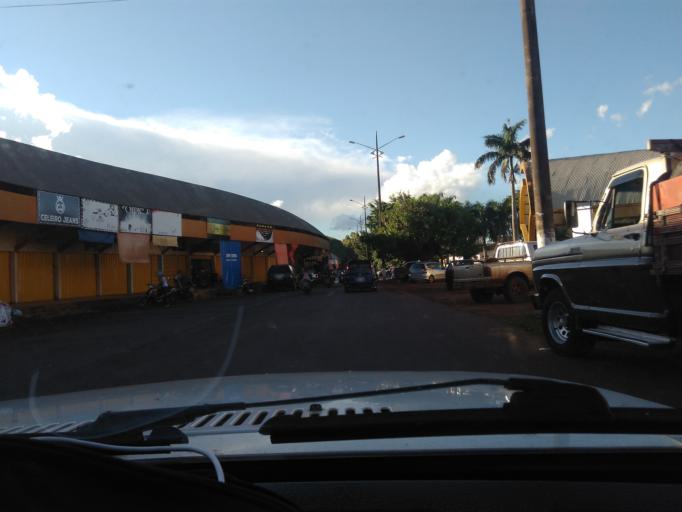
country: BR
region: Mato Grosso do Sul
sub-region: Ponta Pora
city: Ponta Pora
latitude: -22.5378
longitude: -55.7314
